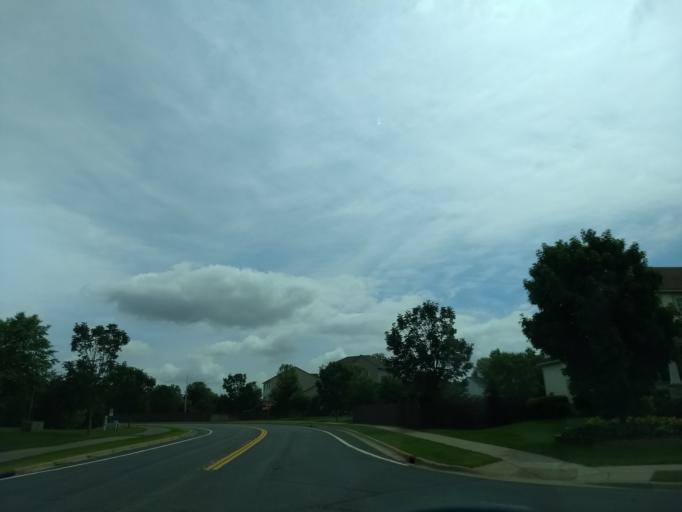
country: US
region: Minnesota
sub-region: Dakota County
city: Rosemount
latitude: 44.7437
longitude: -93.0986
